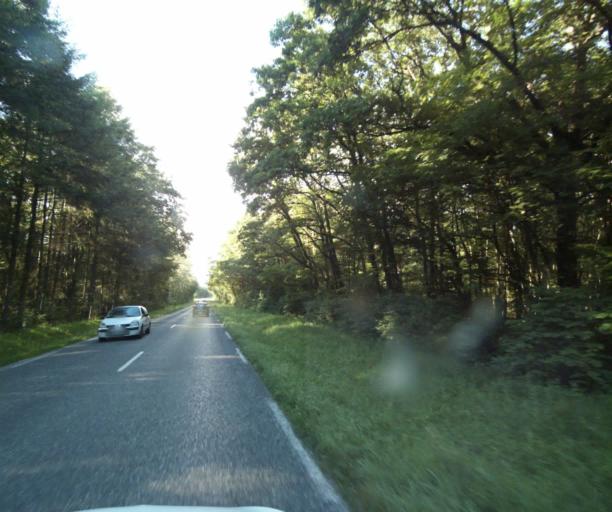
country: FR
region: Rhone-Alpes
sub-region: Departement de la Haute-Savoie
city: Messery
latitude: 46.3318
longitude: 6.2921
